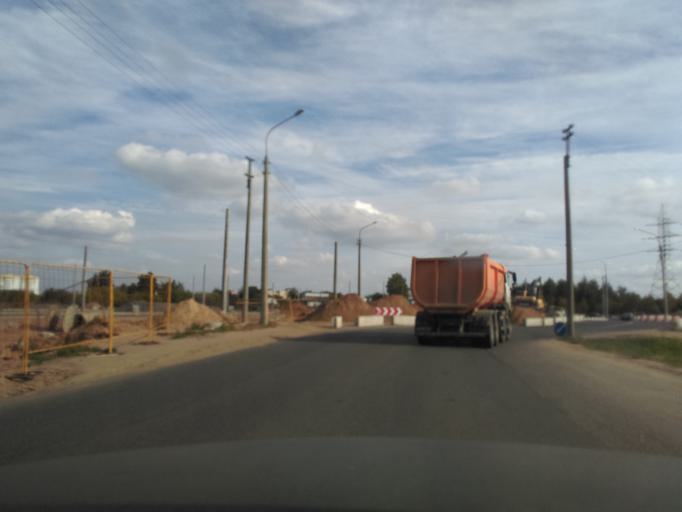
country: BY
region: Minsk
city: Machulishchy
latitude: 53.8375
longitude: 27.5970
